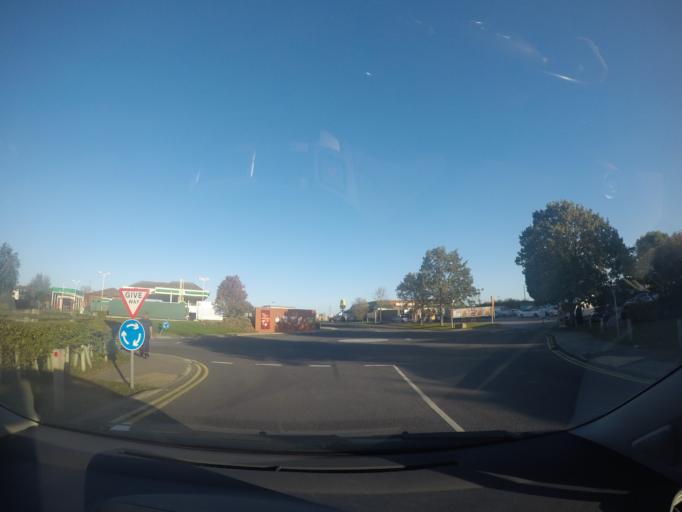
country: GB
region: England
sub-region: City of York
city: Askham Richard
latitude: 53.9057
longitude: -1.1858
